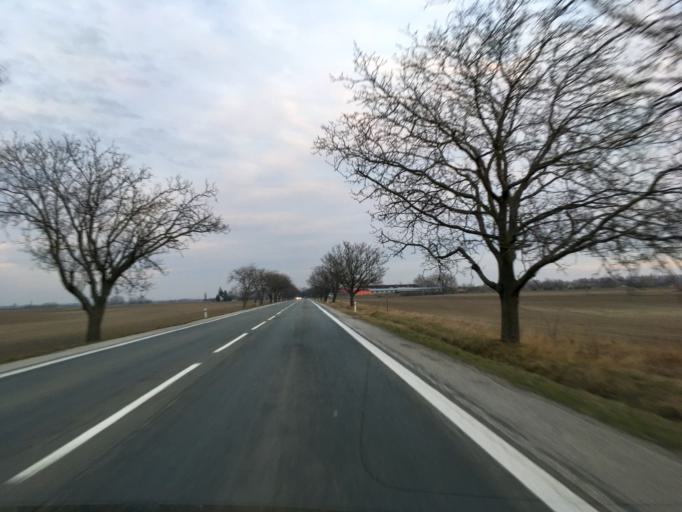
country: HU
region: Komarom-Esztergom
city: Acs
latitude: 47.7666
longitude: 18.0059
